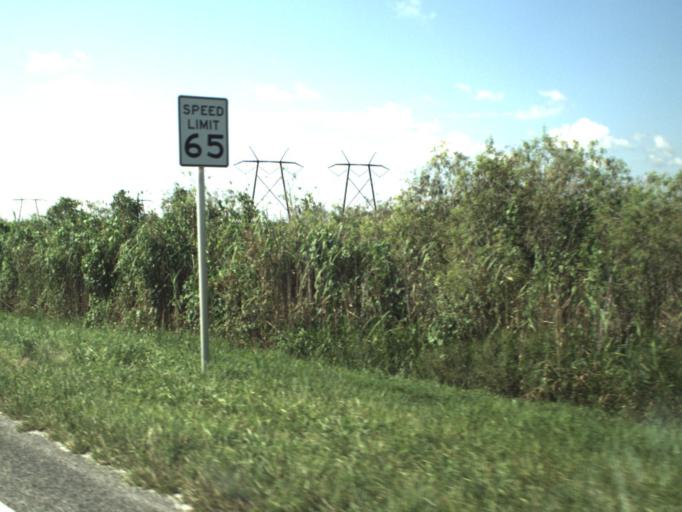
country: US
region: Florida
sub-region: Broward County
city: Weston
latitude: 26.2845
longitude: -80.4992
